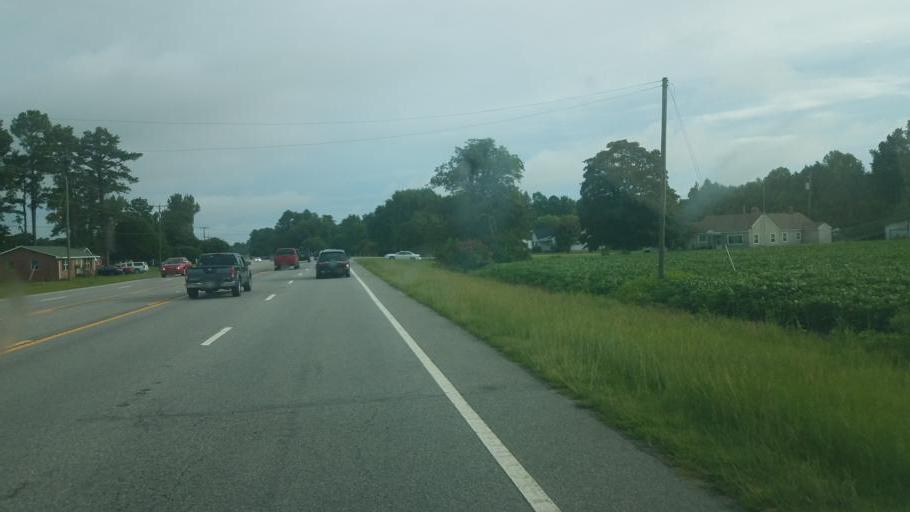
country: US
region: North Carolina
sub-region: Currituck County
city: Currituck
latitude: 36.4267
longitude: -76.0066
